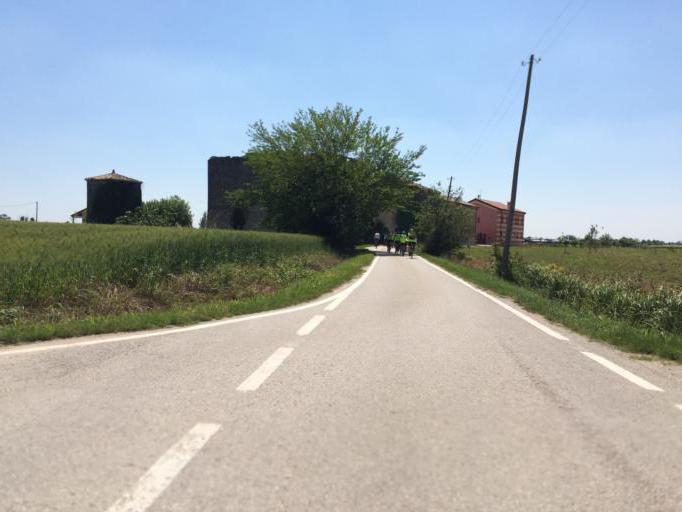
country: IT
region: Veneto
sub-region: Provincia di Vicenza
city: Sossano
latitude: 45.3424
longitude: 11.4994
